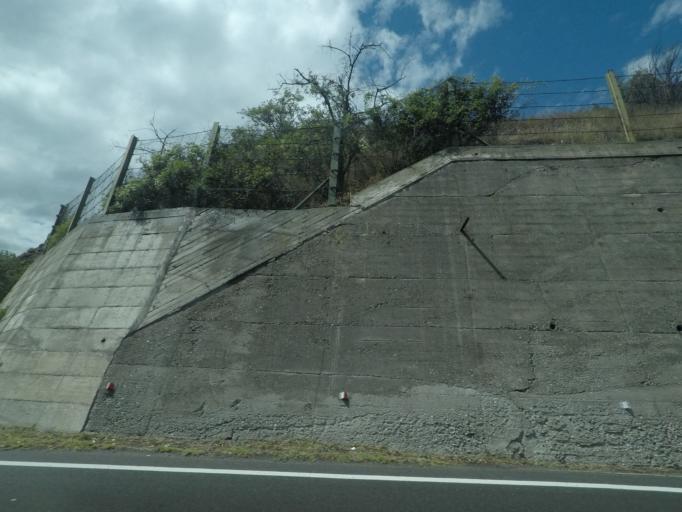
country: IT
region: Aosta Valley
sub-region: Valle d'Aosta
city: Villeneuve
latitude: 45.7038
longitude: 7.2052
